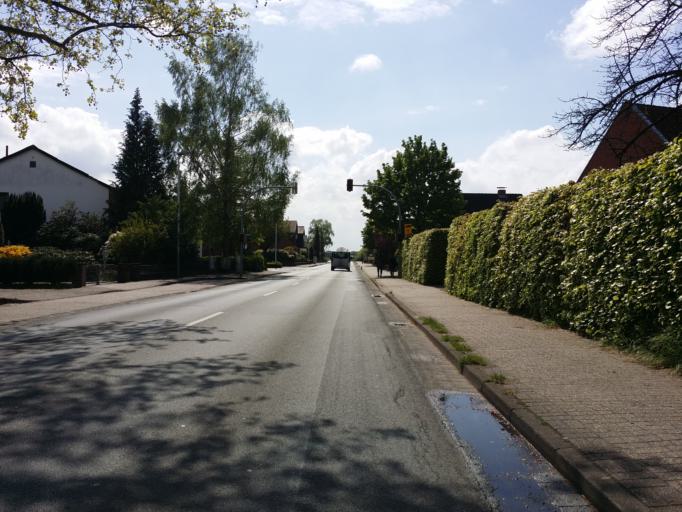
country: DE
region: Lower Saxony
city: Stuhr
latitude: 53.0260
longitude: 8.7464
